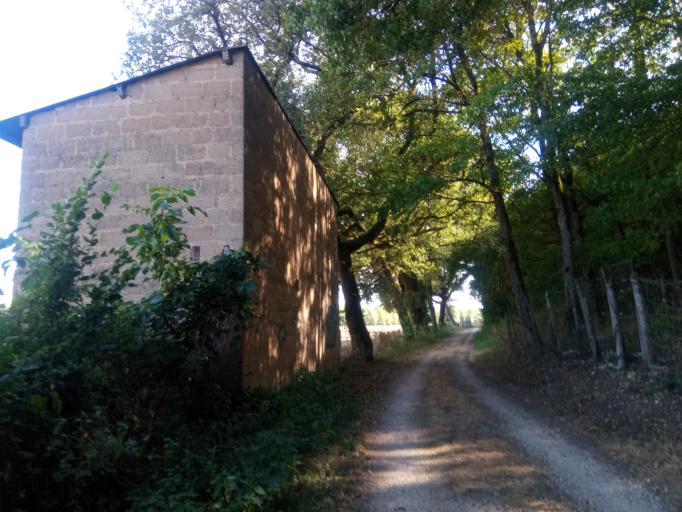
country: FR
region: Poitou-Charentes
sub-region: Departement de la Vienne
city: Saint-Savin
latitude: 46.5564
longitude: 0.8647
